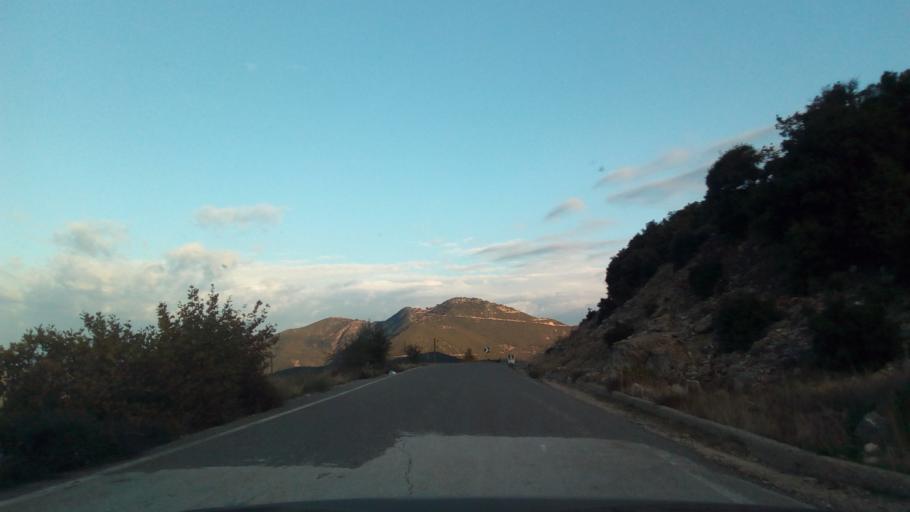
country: GR
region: West Greece
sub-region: Nomos Aitolias kai Akarnanias
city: Nafpaktos
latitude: 38.5081
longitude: 21.8343
